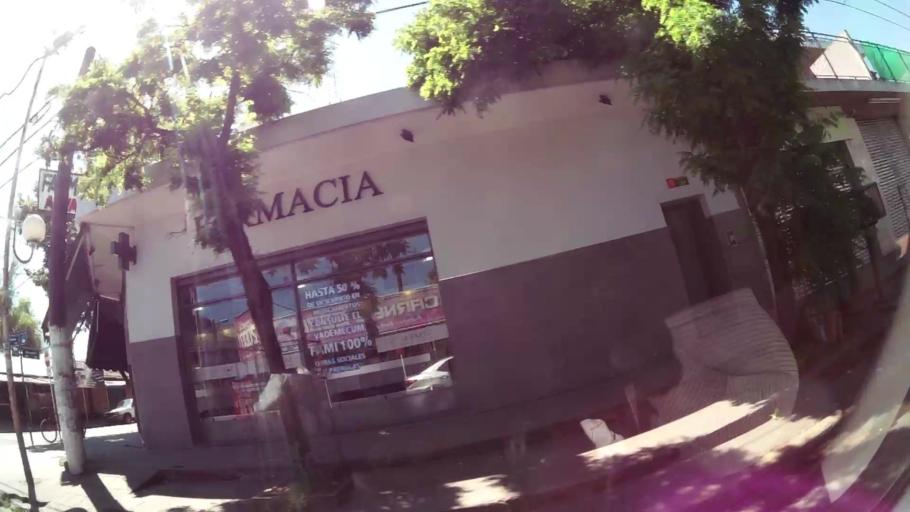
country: AR
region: Buenos Aires
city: Hurlingham
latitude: -34.5023
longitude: -58.6671
